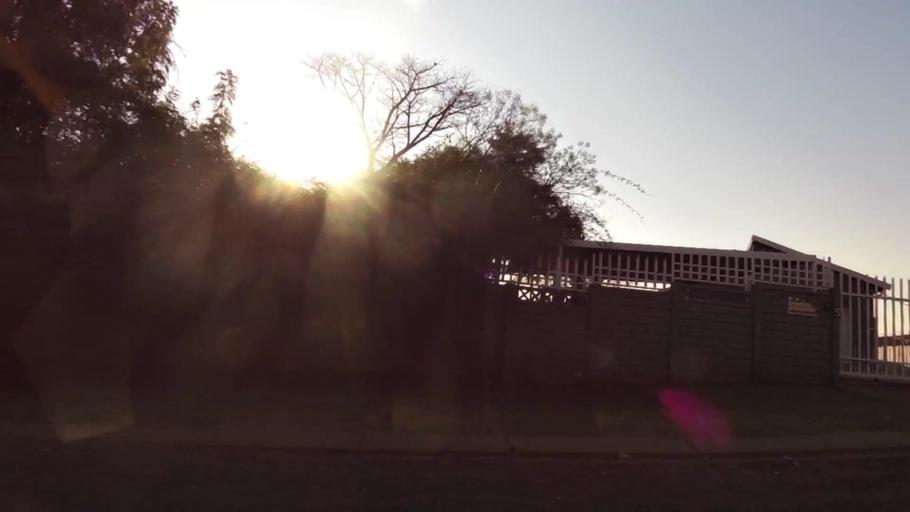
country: ZA
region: Gauteng
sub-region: City of Johannesburg Metropolitan Municipality
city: Soweto
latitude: -26.2814
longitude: 27.9607
